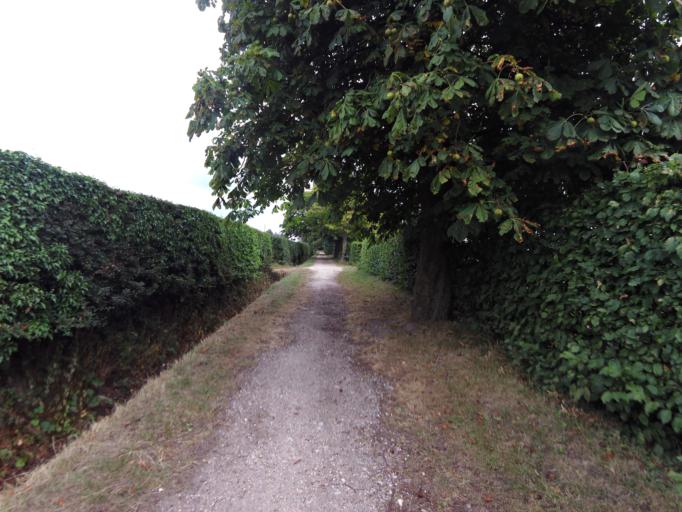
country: GB
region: England
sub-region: Hertfordshire
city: Shenley AV
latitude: 51.7096
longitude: -0.2788
